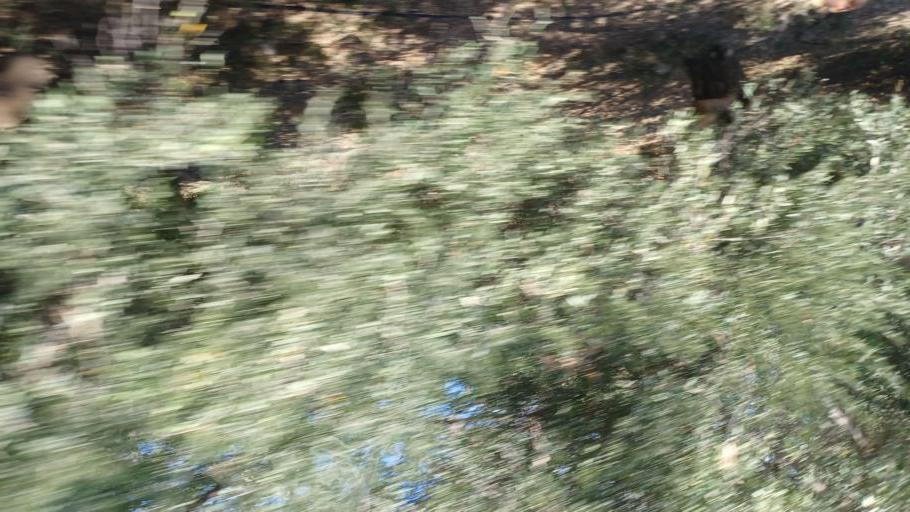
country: CY
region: Pafos
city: Polis
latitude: 35.0438
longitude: 32.4315
